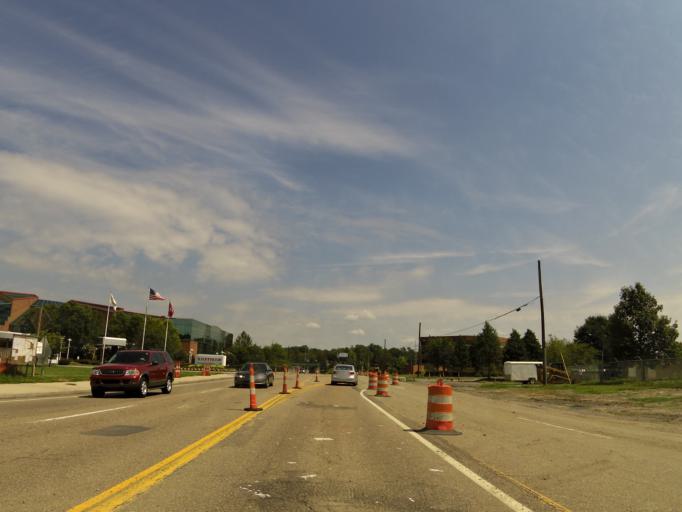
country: US
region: Tennessee
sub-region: Sullivan County
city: Kingsport
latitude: 36.5337
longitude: -82.5511
